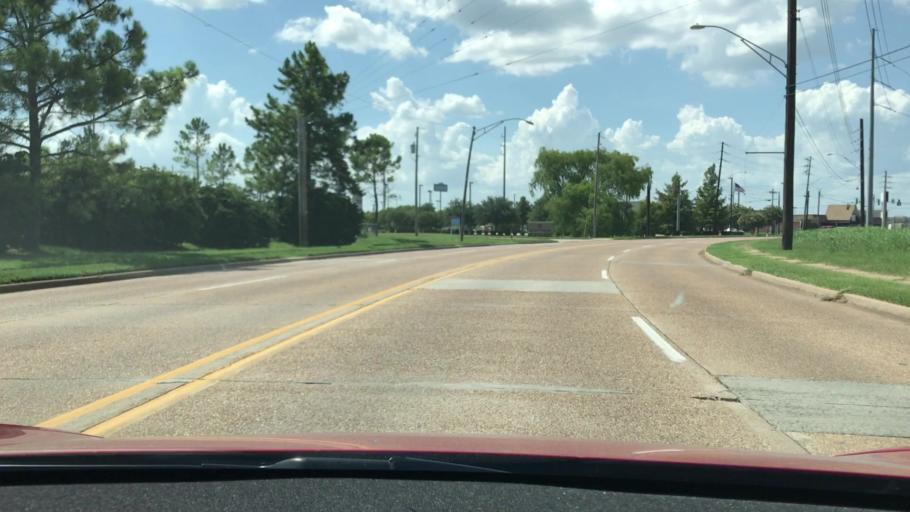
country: US
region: Louisiana
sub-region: Bossier Parish
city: Bossier City
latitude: 32.4416
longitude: -93.7131
